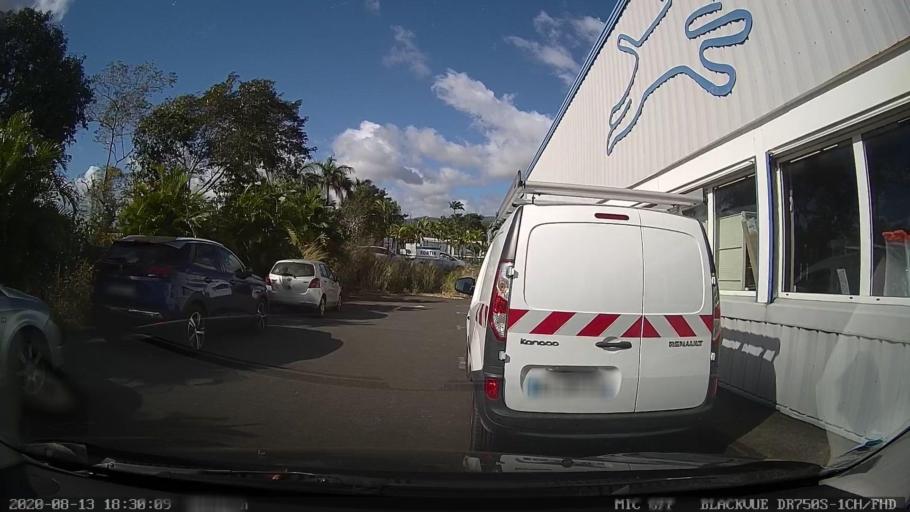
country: RE
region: Reunion
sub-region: Reunion
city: Sainte-Marie
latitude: -20.8988
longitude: 55.5372
